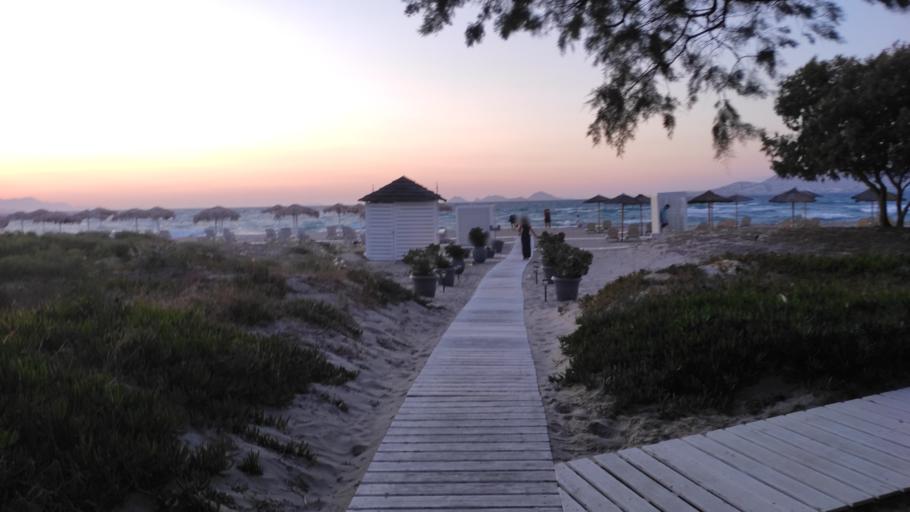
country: GR
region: South Aegean
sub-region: Nomos Dodekanisou
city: Kos
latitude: 36.9148
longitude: 27.2772
